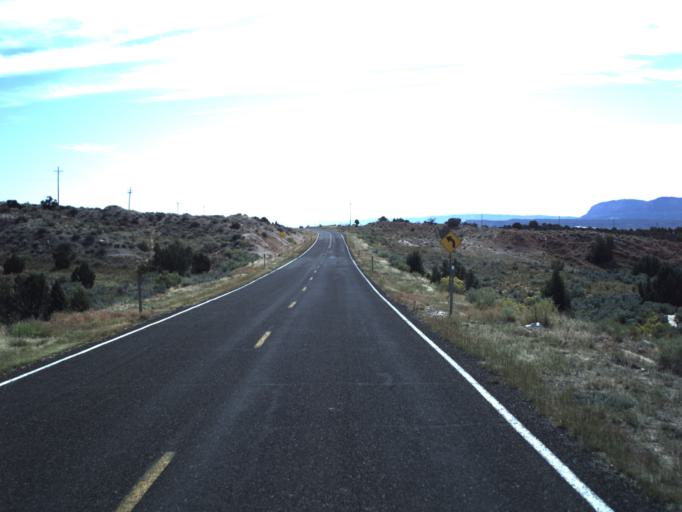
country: US
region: Utah
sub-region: Wayne County
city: Loa
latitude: 37.7460
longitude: -111.5625
